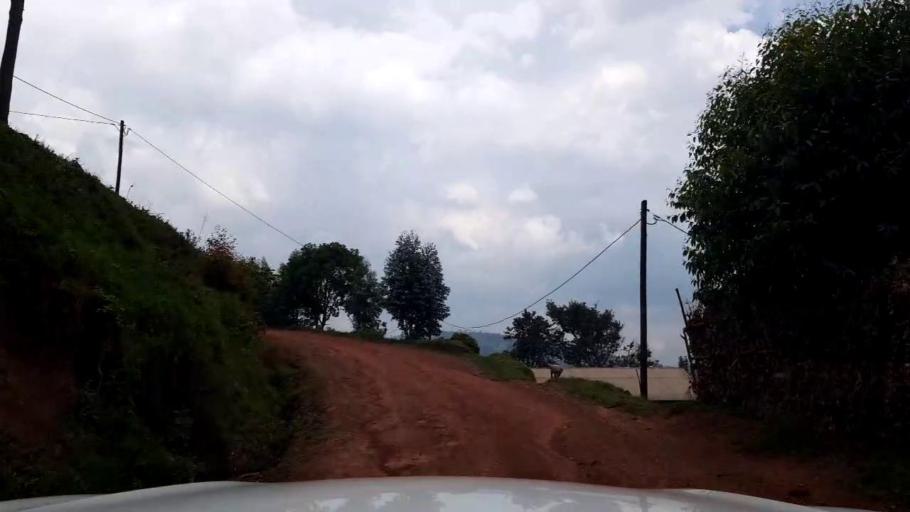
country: RW
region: Northern Province
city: Byumba
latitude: -1.4887
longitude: 29.9115
